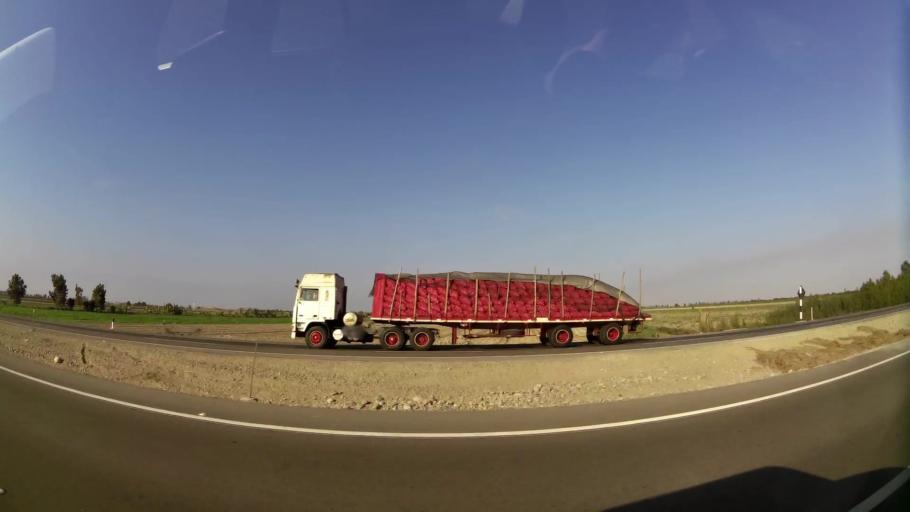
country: PE
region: Ica
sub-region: Provincia de Chincha
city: Chincha Baja
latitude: -13.5089
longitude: -76.1850
